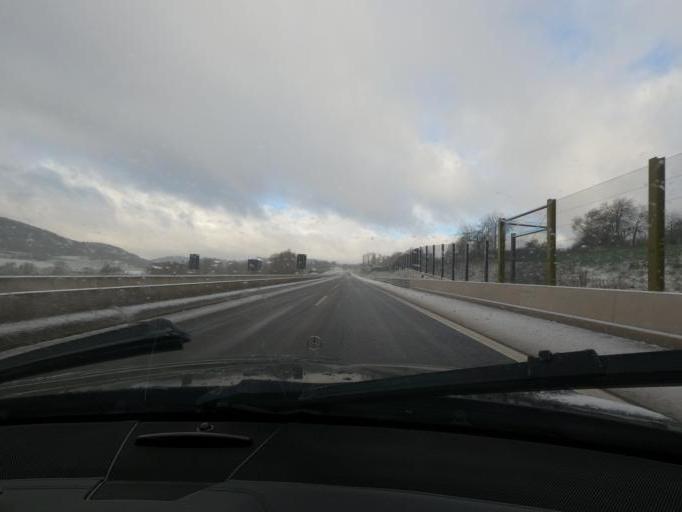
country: DE
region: Hesse
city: Waldkappel
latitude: 51.1515
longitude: 9.9070
